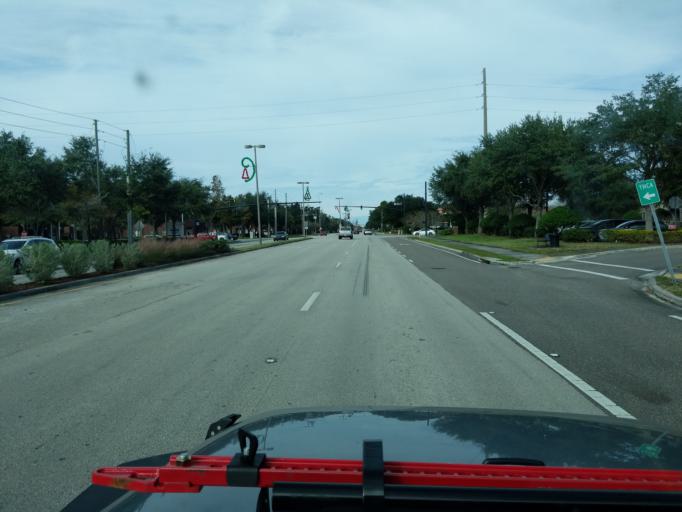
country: US
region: Florida
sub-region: Orange County
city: Gotha
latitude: 28.5288
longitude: -81.5417
